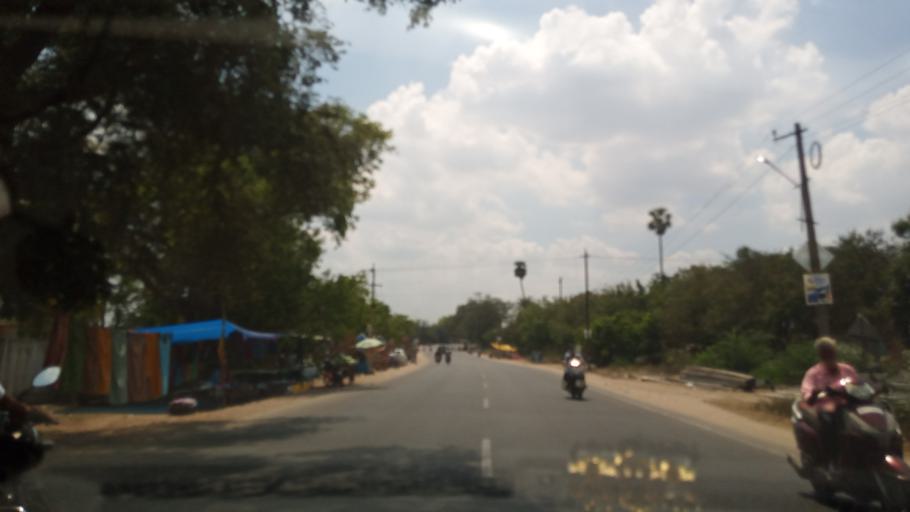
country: IN
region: Tamil Nadu
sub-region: Vellore
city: Walajapet
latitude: 12.9254
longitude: 79.3550
